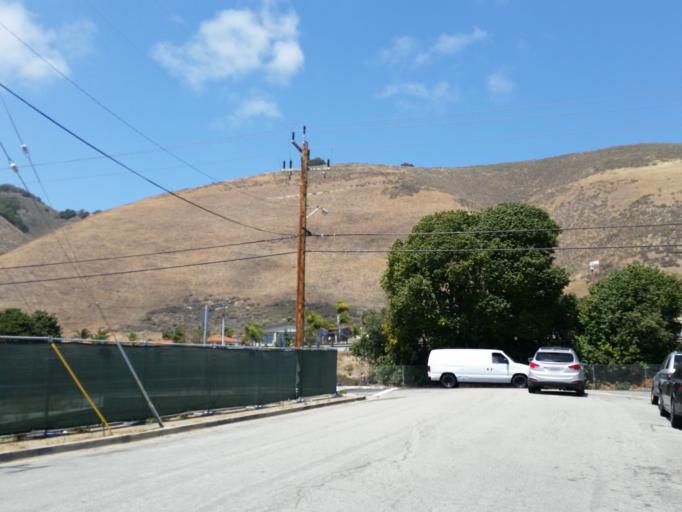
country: US
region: California
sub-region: San Luis Obispo County
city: Pismo Beach
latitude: 35.1560
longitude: -120.6692
